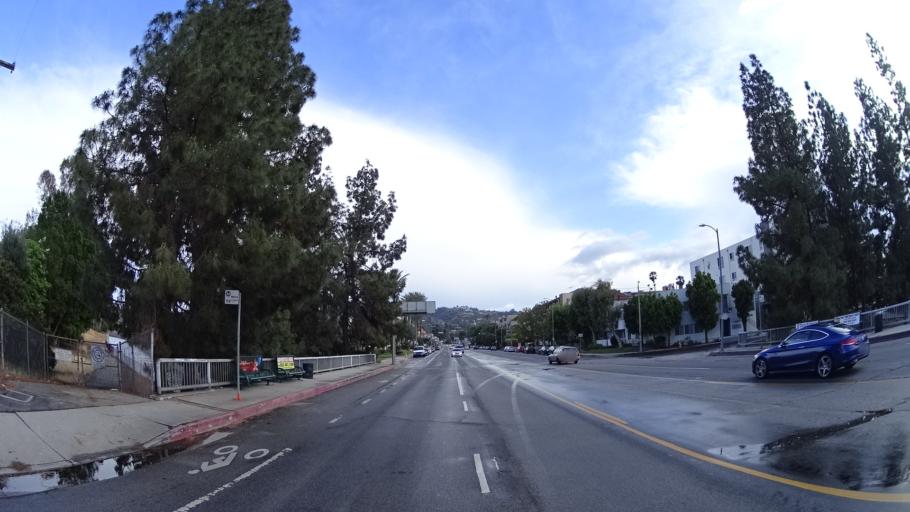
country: US
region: California
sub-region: Los Angeles County
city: Sherman Oaks
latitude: 34.1543
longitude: -118.4312
